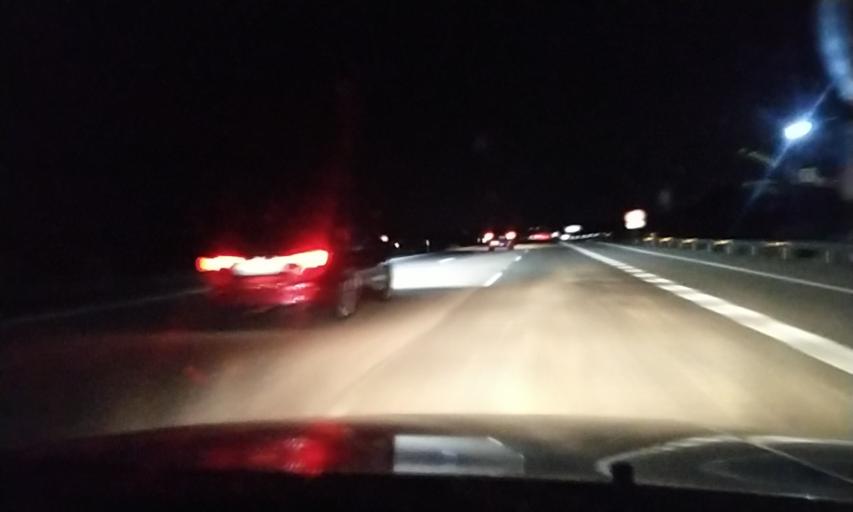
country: ES
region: Castille and Leon
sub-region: Provincia de Zamora
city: Benavente
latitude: 42.0380
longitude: -5.6727
